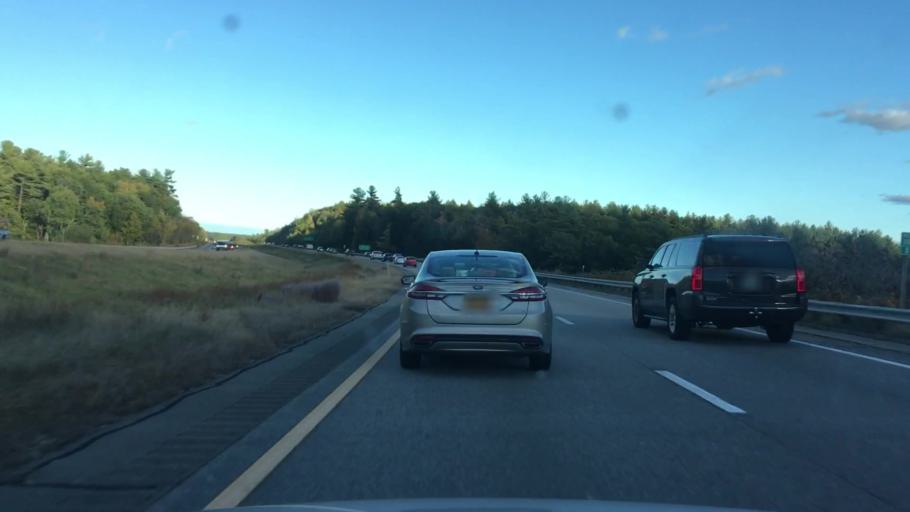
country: US
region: New Hampshire
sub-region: Rockingham County
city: Raymond
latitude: 43.0219
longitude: -71.2283
